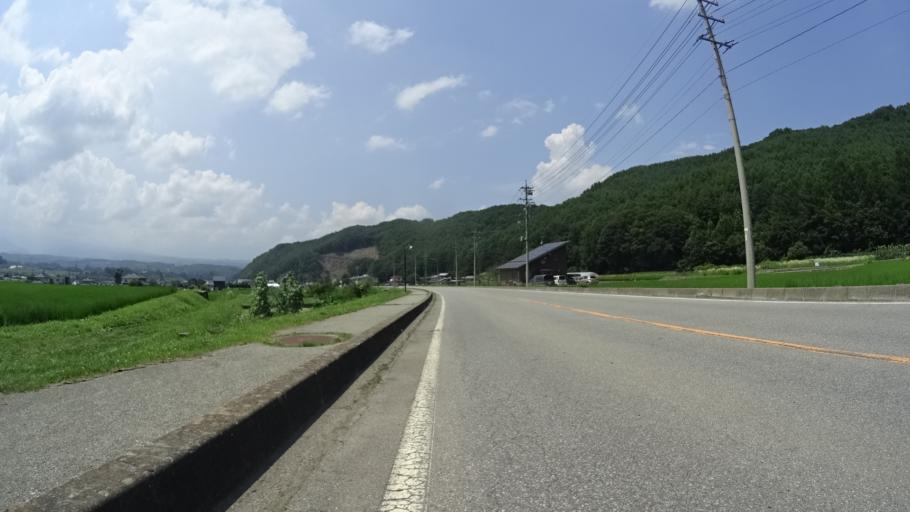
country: JP
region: Nagano
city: Saku
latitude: 36.1534
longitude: 138.5042
